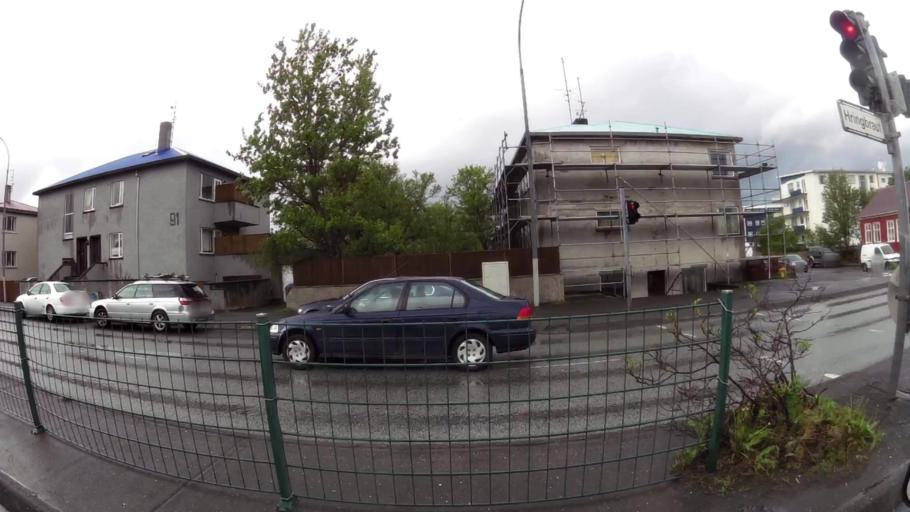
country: IS
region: Capital Region
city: Seltjarnarnes
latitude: 64.1475
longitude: -21.9574
